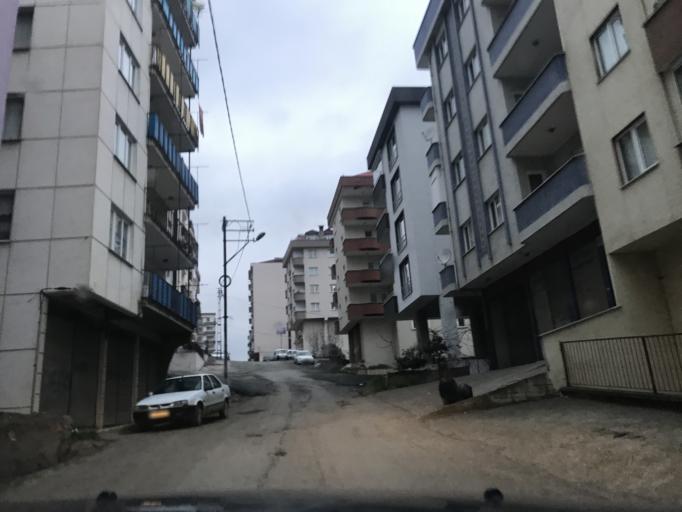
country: TR
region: Trabzon
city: Akcaabat
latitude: 41.0155
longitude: 39.5891
